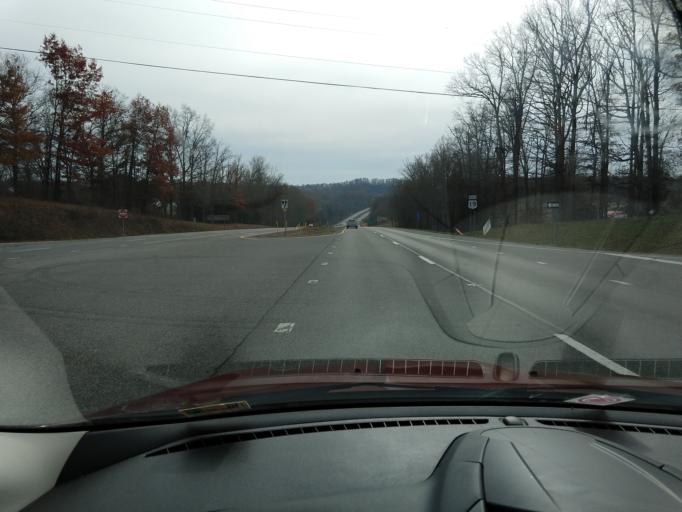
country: US
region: West Virginia
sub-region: Nicholas County
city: Summersville
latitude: 38.2831
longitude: -80.8336
